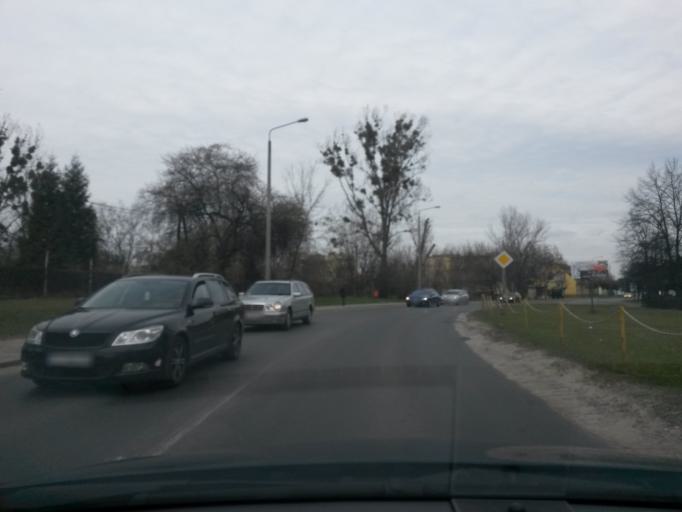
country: PL
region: Greater Poland Voivodeship
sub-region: Poznan
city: Poznan
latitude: 52.4433
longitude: 16.9457
